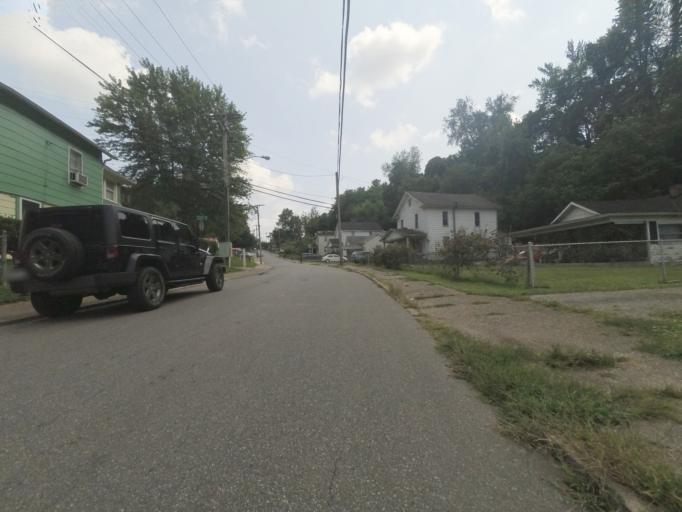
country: US
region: West Virginia
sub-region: Cabell County
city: Huntington
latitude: 38.4166
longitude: -82.4053
